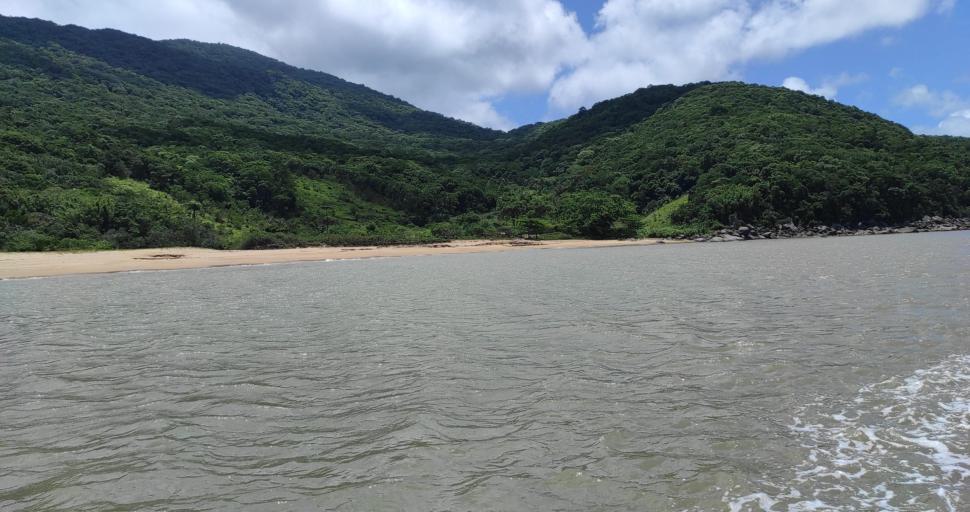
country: BR
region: Santa Catarina
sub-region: Porto Belo
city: Porto Belo
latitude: -27.2044
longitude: -48.5716
